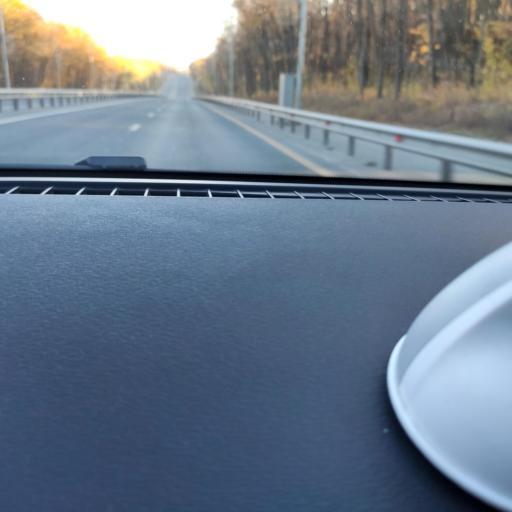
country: RU
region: Samara
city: Petra-Dubrava
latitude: 53.2917
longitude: 50.2475
